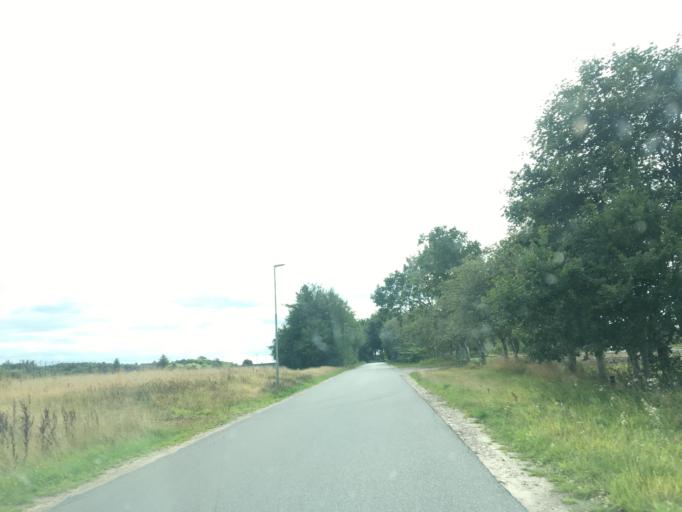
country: DK
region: North Denmark
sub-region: Vesthimmerland Kommune
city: Farso
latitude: 56.8770
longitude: 9.4000
